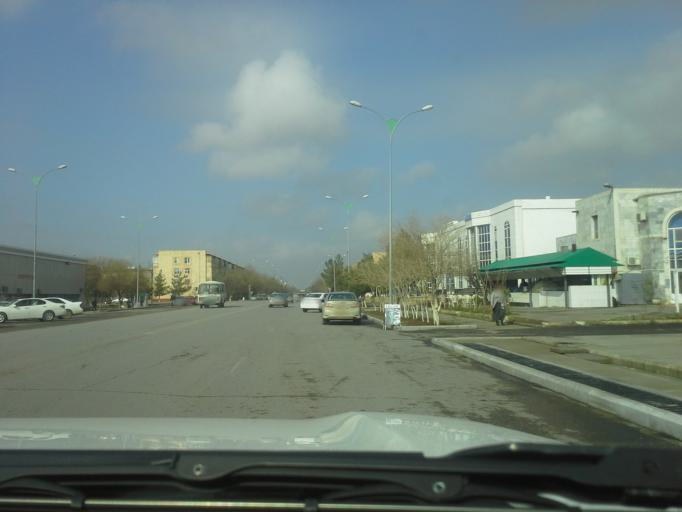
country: TM
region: Mary
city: Mary
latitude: 37.5919
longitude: 61.8355
